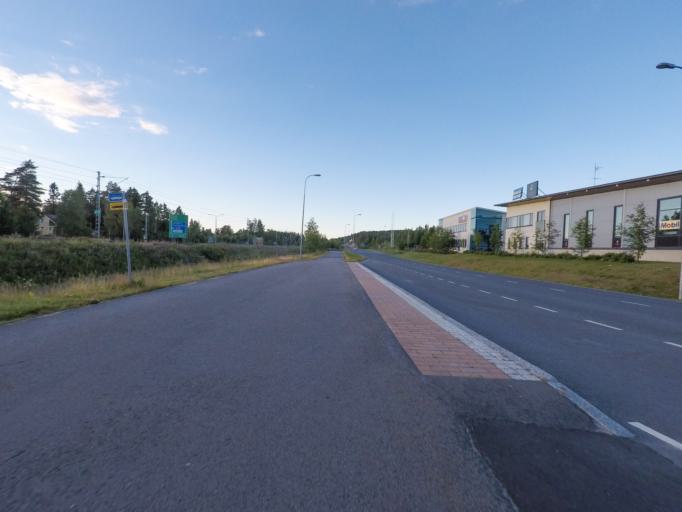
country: FI
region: Northern Savo
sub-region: Kuopio
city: Kuopio
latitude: 62.9631
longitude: 27.6969
